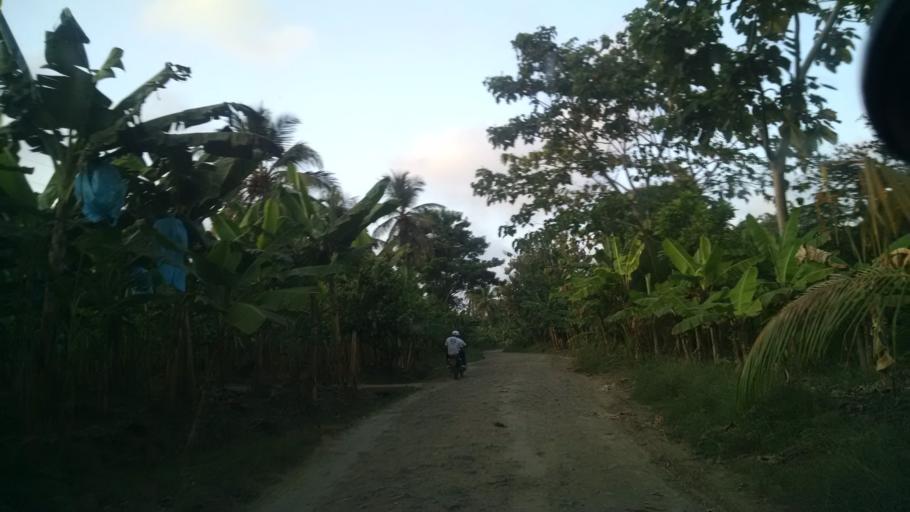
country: CO
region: Antioquia
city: San Juan de Uraba
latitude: 8.7276
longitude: -76.6051
